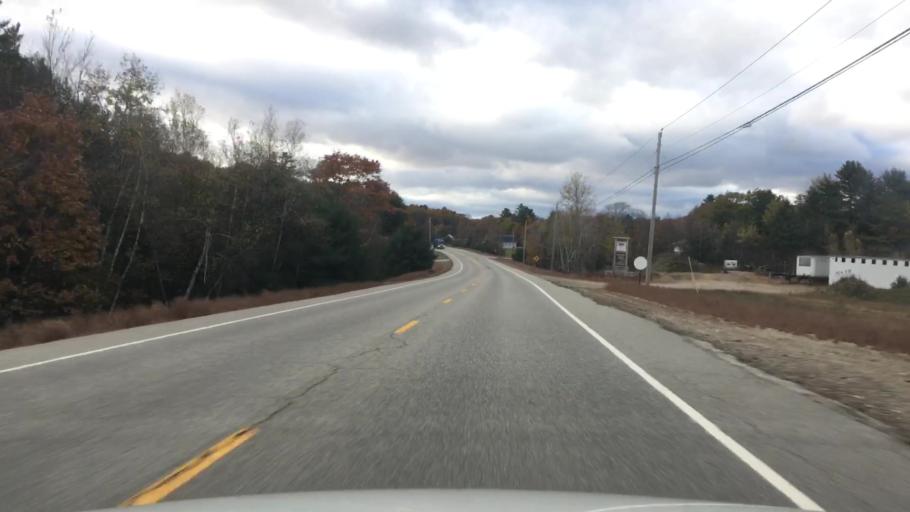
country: US
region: Maine
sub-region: Androscoggin County
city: Livermore
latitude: 44.4106
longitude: -70.2801
